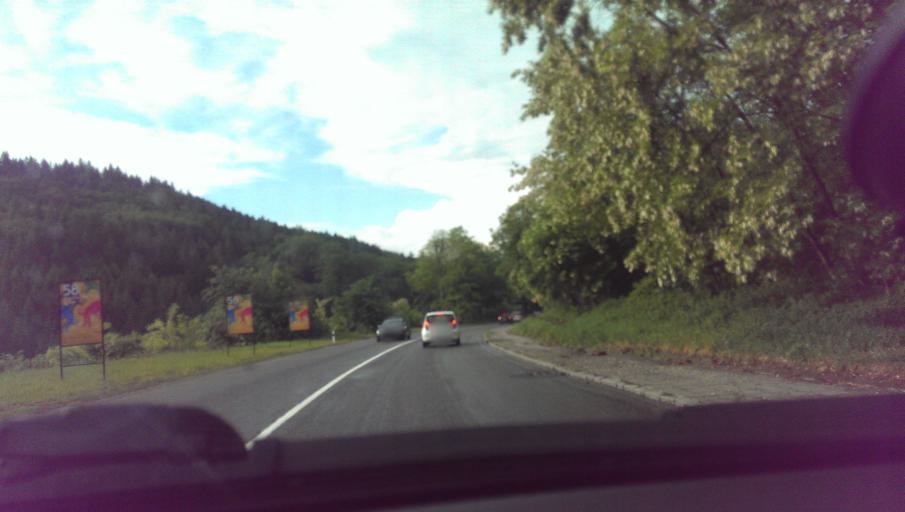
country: CZ
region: Zlin
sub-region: Okres Zlin
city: Zlin
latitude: 49.2079
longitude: 17.6606
